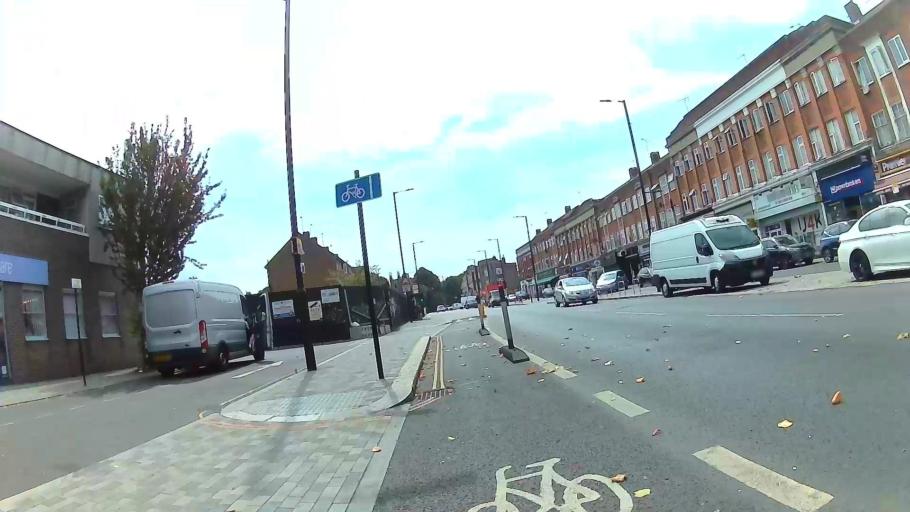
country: GB
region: England
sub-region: Hertfordshire
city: Waltham Cross
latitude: 51.6586
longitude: -0.0471
